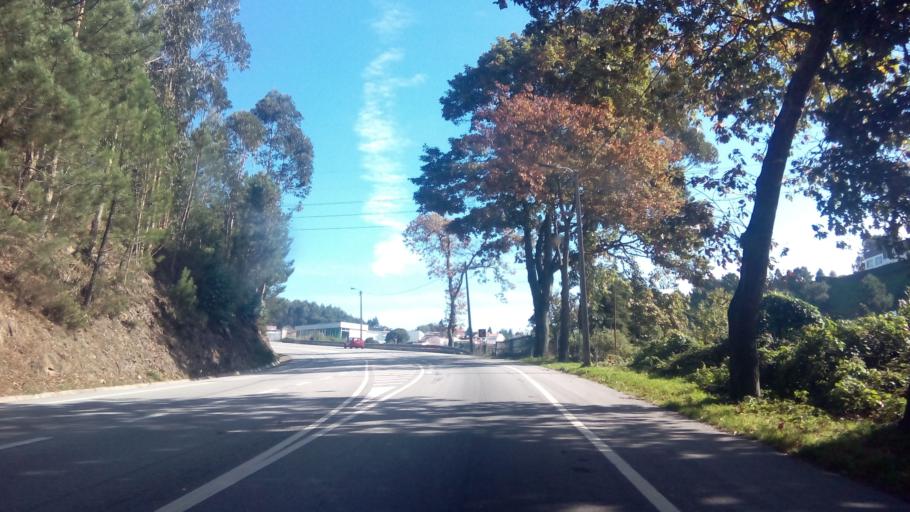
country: PT
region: Porto
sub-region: Paredes
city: Gandra
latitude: 41.1925
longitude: -8.4132
